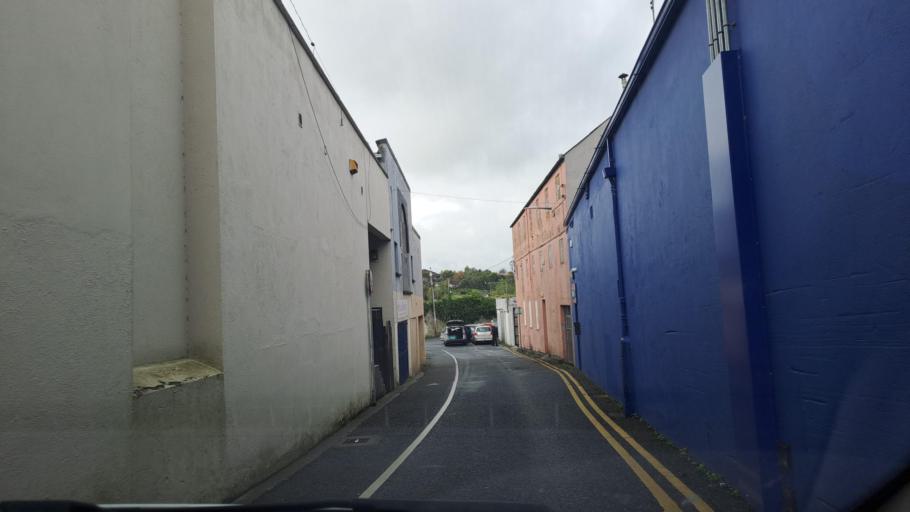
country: IE
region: Ulster
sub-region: County Monaghan
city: Carrickmacross
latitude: 53.9763
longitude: -6.7193
